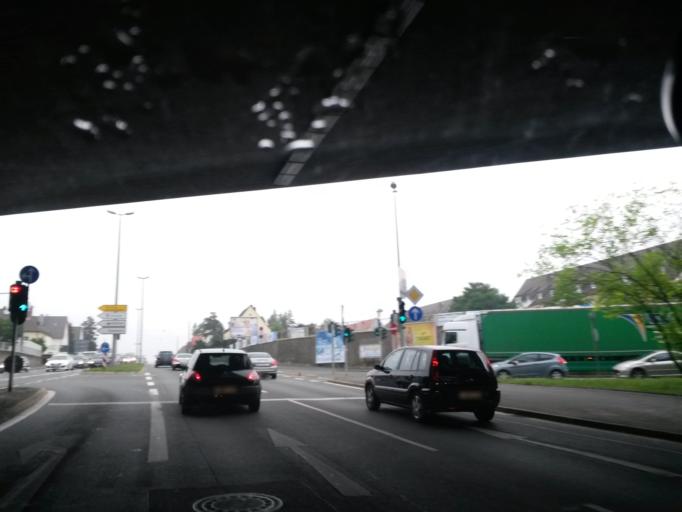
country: DE
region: Bavaria
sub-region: Regierungsbezirk Mittelfranken
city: Furth
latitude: 49.4521
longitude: 10.9895
